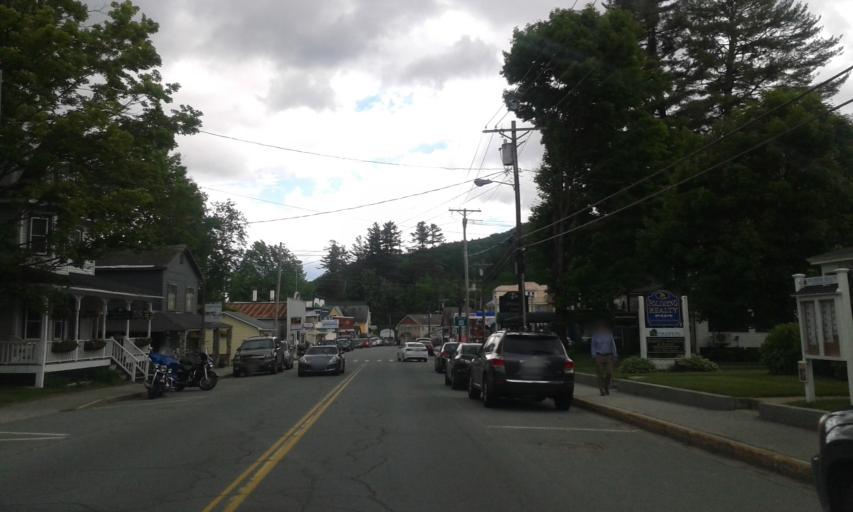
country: US
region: New Hampshire
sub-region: Grafton County
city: Woodstock
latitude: 44.0330
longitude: -71.6866
